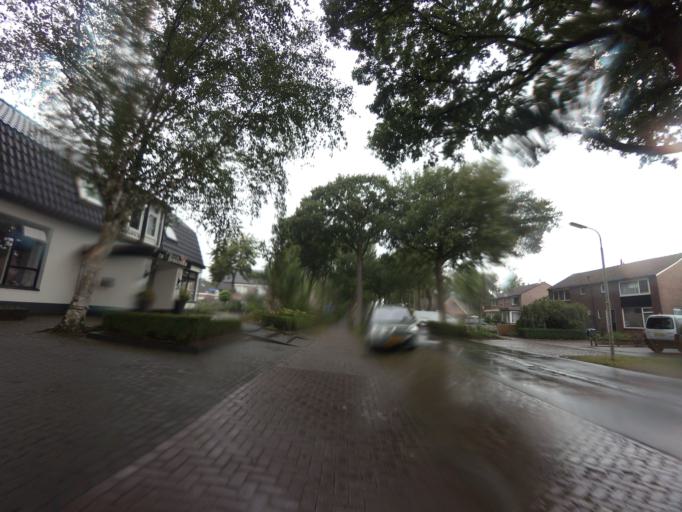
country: NL
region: Drenthe
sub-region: Gemeente Hoogeveen
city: Hoogeveen
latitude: 52.6680
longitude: 6.4999
